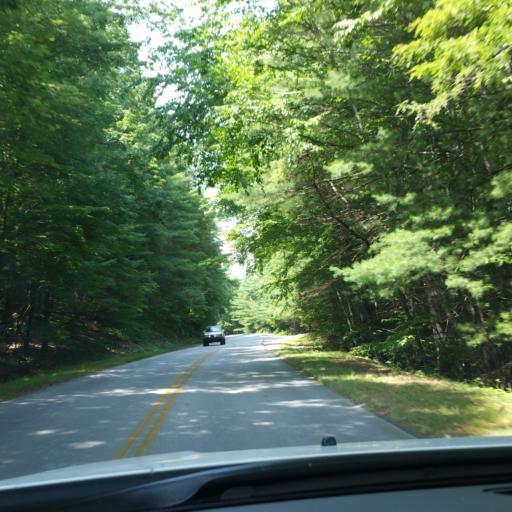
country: US
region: North Carolina
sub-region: Buncombe County
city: Biltmore Forest
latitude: 35.5404
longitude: -82.4988
